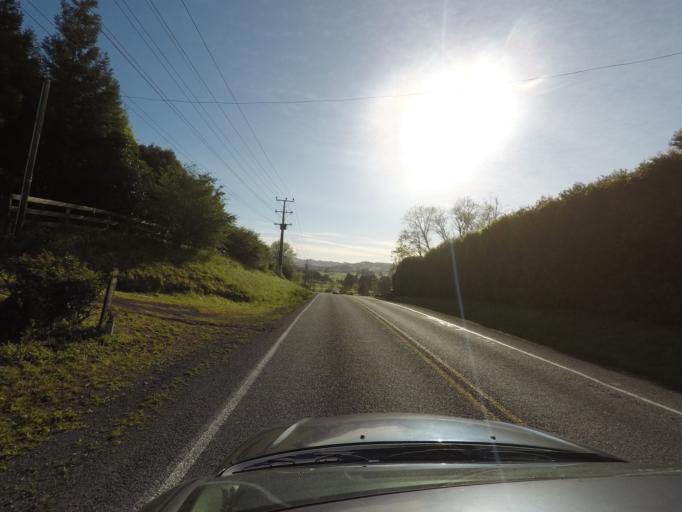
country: NZ
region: Auckland
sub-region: Auckland
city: Red Hill
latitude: -37.0133
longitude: 174.9484
